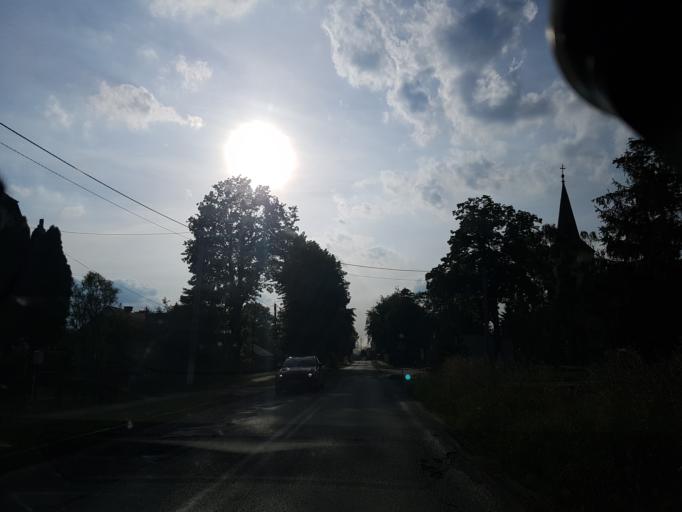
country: PL
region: Lower Silesian Voivodeship
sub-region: Powiat wroclawski
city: Kobierzyce
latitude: 50.9184
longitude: 16.9602
